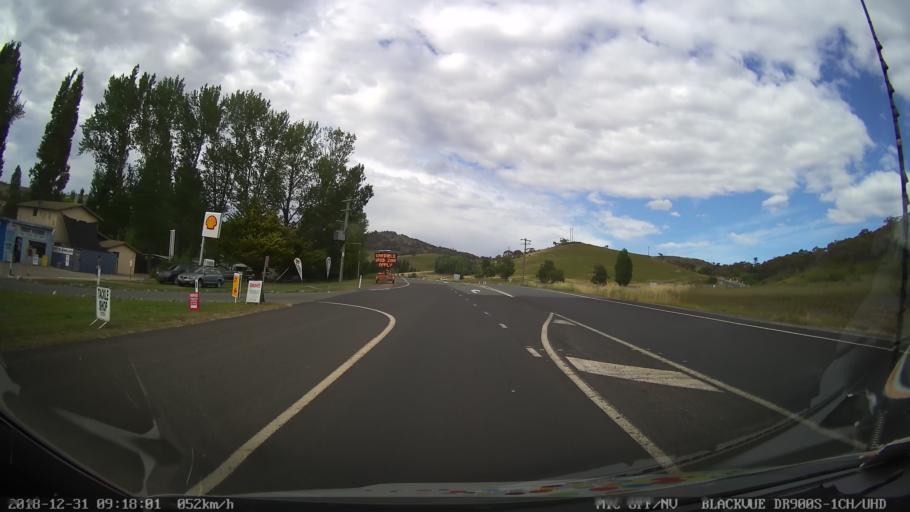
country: AU
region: New South Wales
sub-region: Snowy River
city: Jindabyne
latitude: -36.4098
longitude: 148.5964
